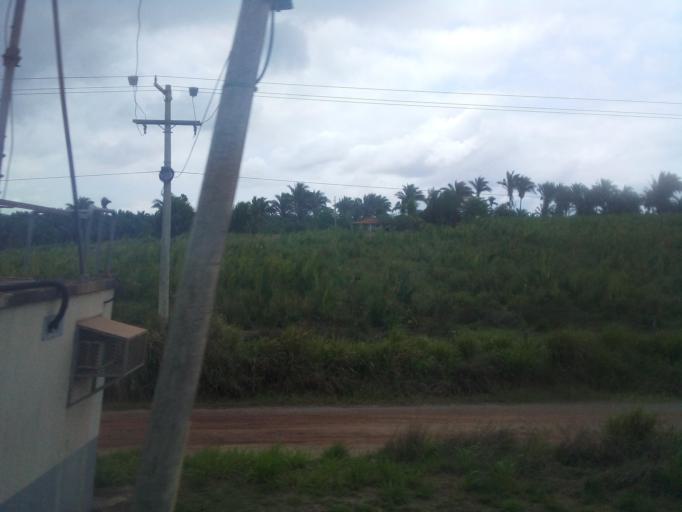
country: BR
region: Maranhao
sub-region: Santa Ines
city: Santa Ines
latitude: -3.7223
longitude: -45.4866
